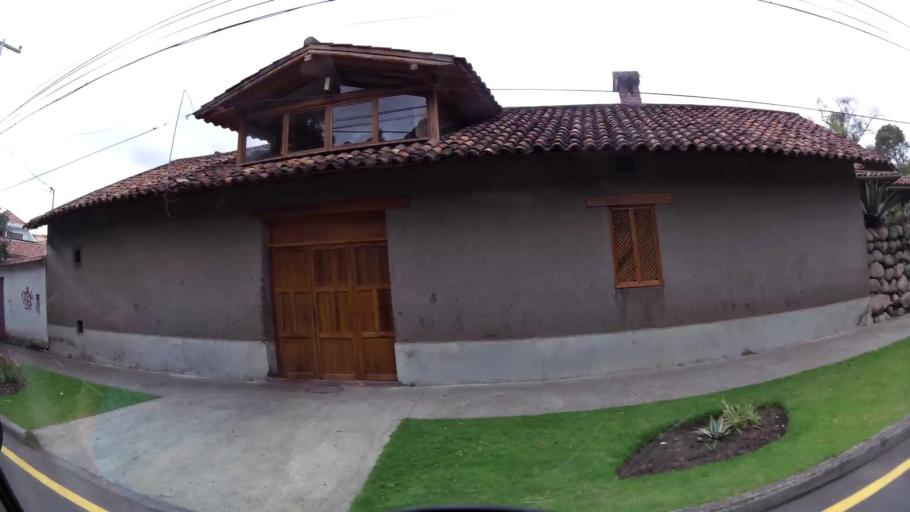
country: EC
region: Azuay
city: Cuenca
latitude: -2.9101
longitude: -79.0177
